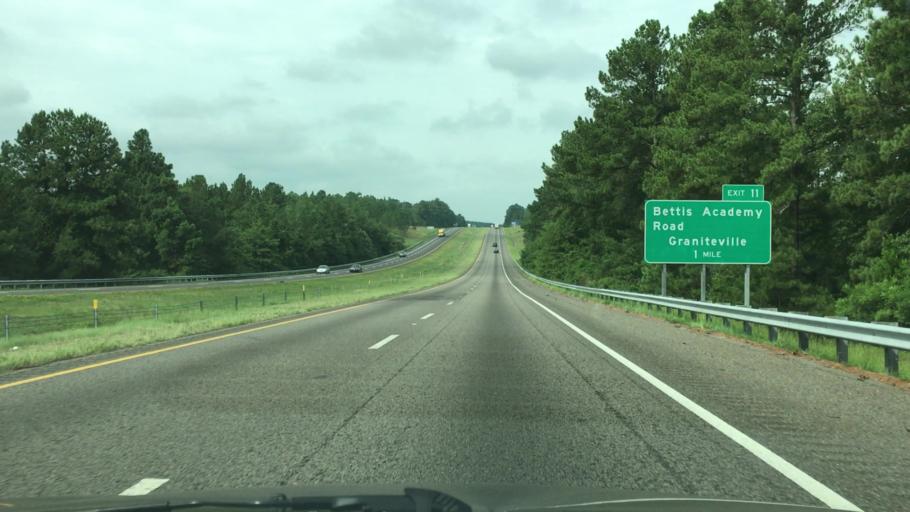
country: US
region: South Carolina
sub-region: Aiken County
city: Graniteville
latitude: 33.6187
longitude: -81.8271
